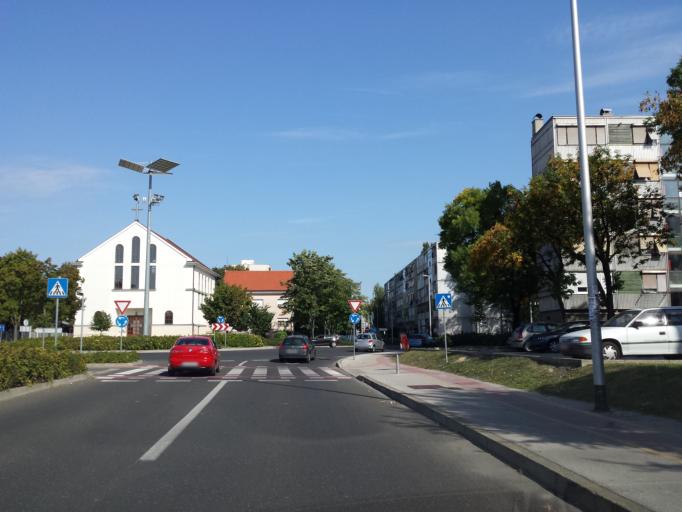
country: HR
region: Grad Zagreb
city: Novi Zagreb
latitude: 45.7694
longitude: 15.9444
